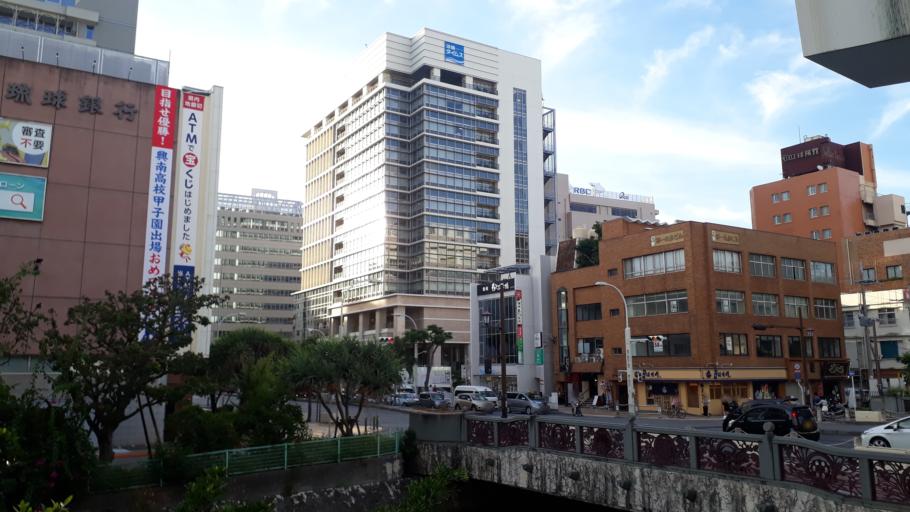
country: JP
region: Okinawa
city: Naha-shi
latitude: 26.2142
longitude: 127.6808
